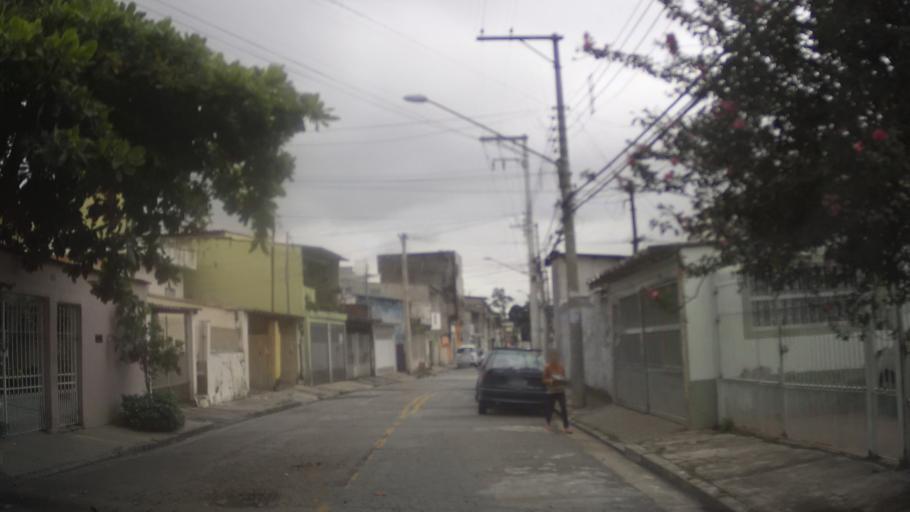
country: BR
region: Sao Paulo
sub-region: Guarulhos
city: Guarulhos
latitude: -23.4521
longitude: -46.5210
